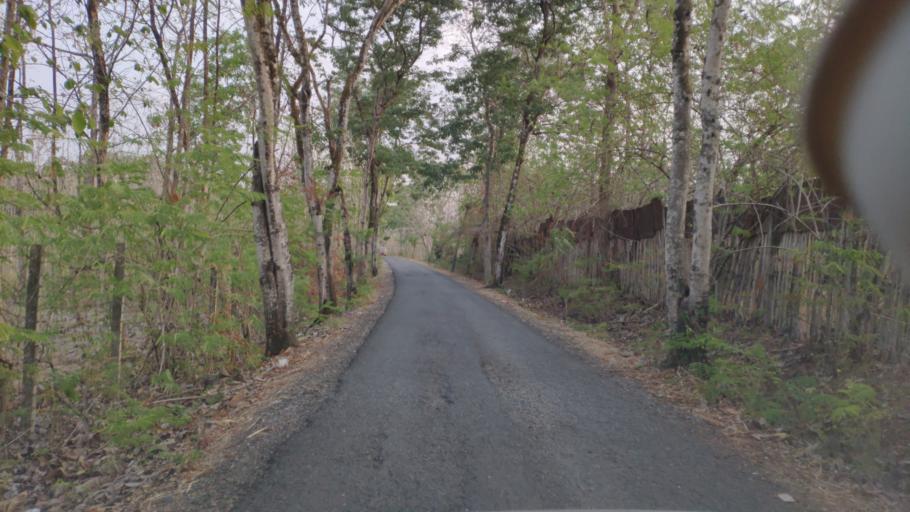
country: ID
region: Central Java
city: Tawangsari
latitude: -6.9756
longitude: 111.3504
